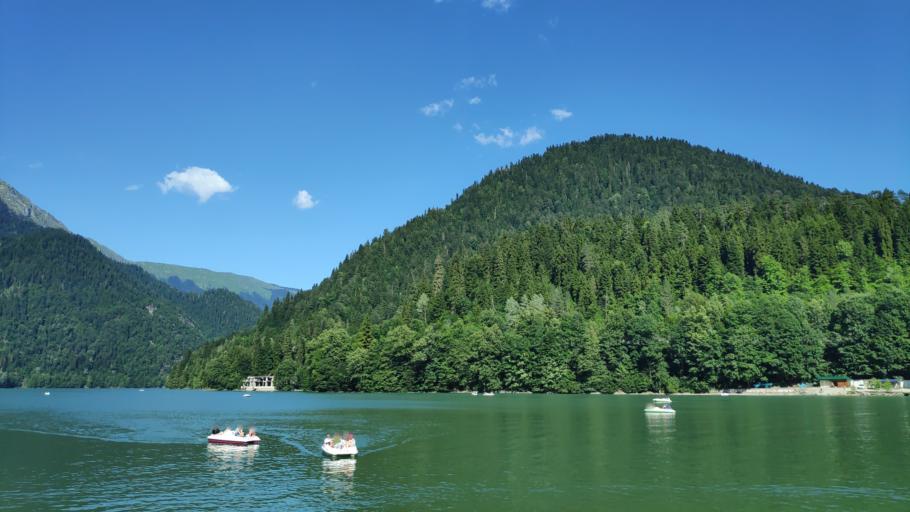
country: GE
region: Abkhazia
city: Gagra
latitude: 43.4734
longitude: 40.5323
